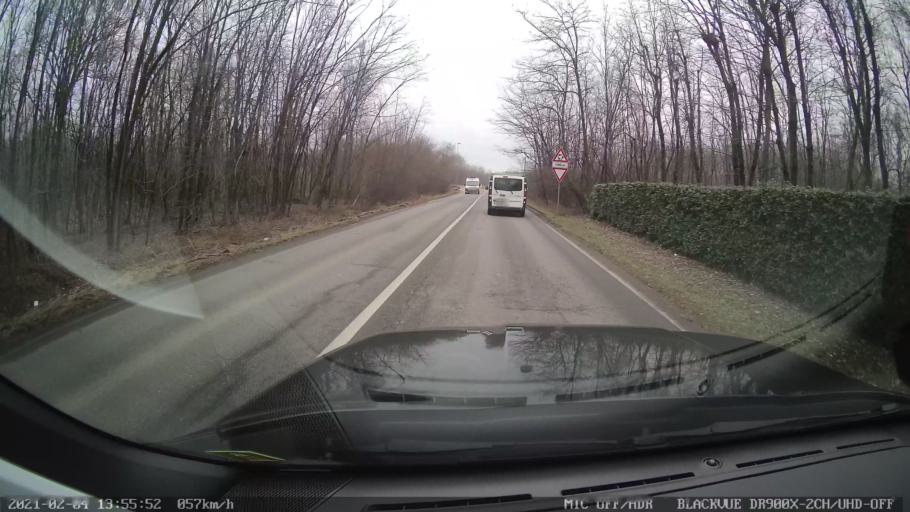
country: IT
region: Lombardy
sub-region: Provincia di Varese
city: Cairate
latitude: 45.6887
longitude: 8.8881
